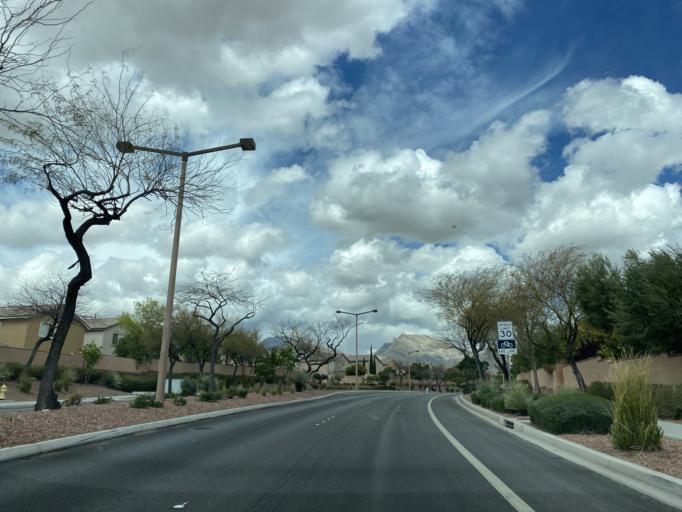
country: US
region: Nevada
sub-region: Clark County
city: Summerlin South
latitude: 36.1799
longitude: -115.3362
